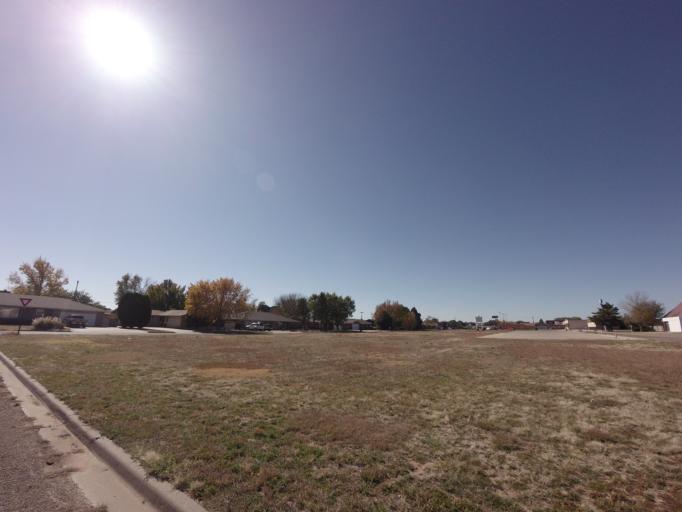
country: US
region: New Mexico
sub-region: Curry County
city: Clovis
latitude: 34.4220
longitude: -103.1926
